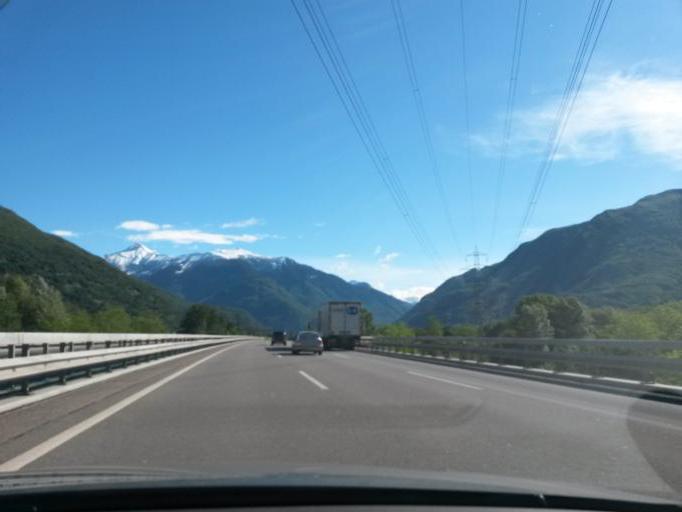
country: CH
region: Ticino
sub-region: Bellinzona District
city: Sementina
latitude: 46.1740
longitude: 8.9934
